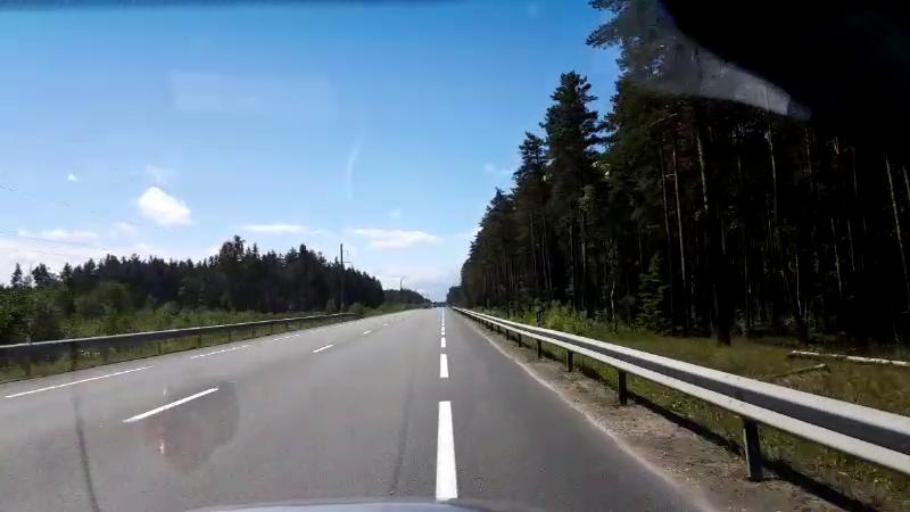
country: LV
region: Saulkrastu
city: Saulkrasti
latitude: 57.2174
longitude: 24.4027
